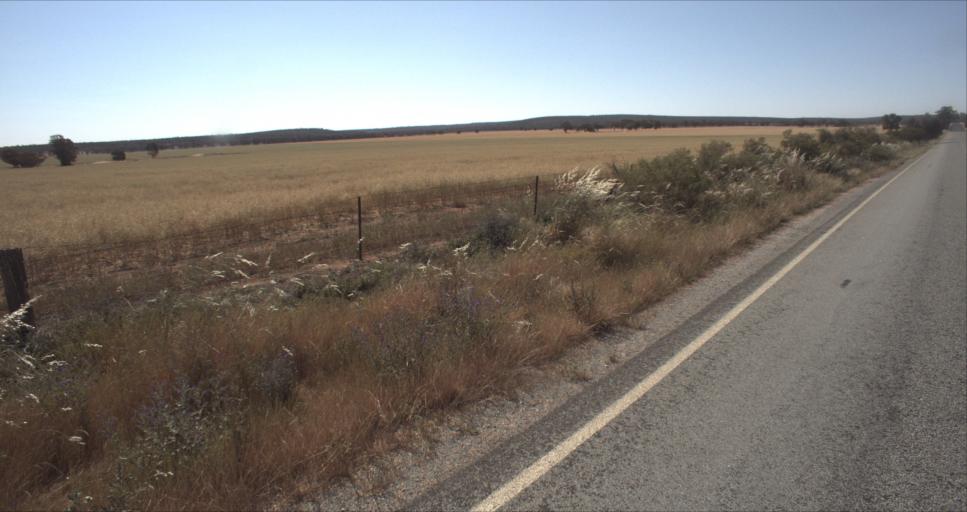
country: AU
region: New South Wales
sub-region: Leeton
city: Leeton
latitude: -34.4589
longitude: 146.4381
